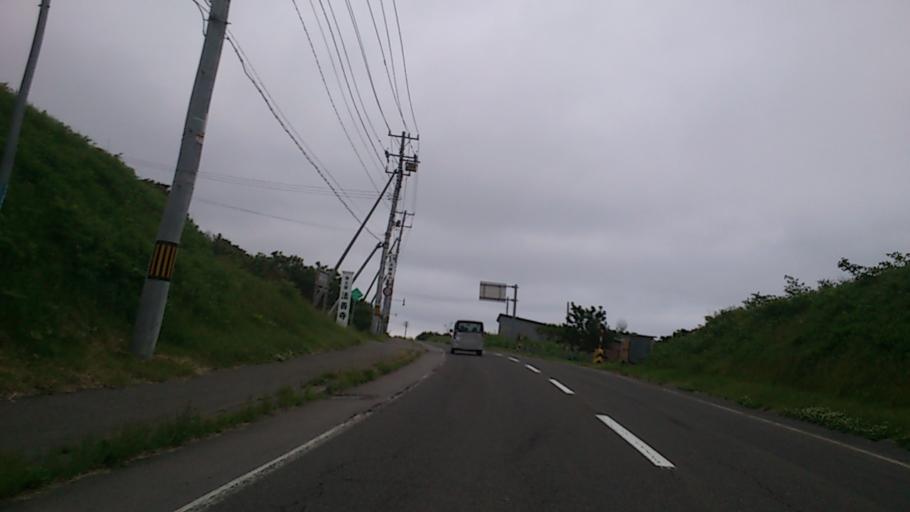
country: JP
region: Hokkaido
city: Iwanai
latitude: 42.7354
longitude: 140.0945
